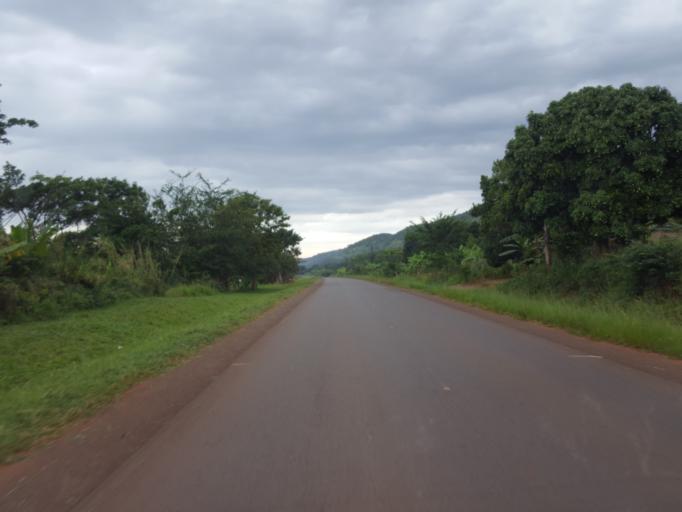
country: UG
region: Central Region
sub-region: Kiboga District
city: Kiboga
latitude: 0.8494
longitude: 31.8731
